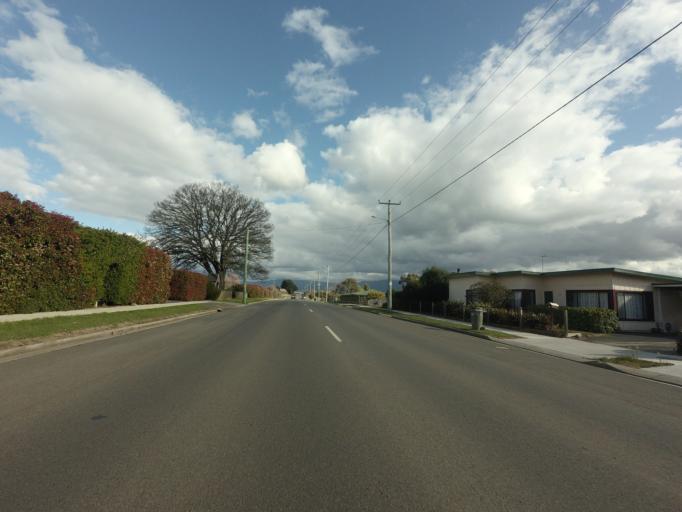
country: AU
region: Tasmania
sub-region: Northern Midlands
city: Longford
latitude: -41.6926
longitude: 147.0789
